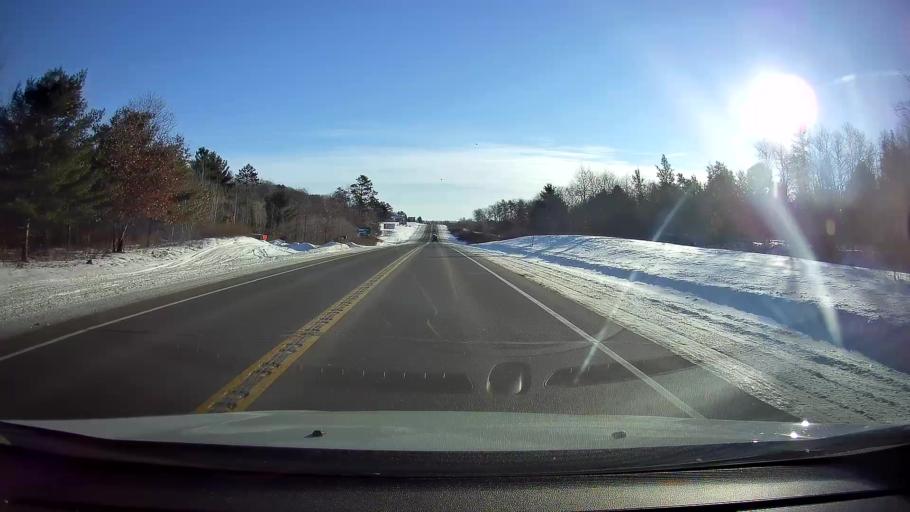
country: US
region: Wisconsin
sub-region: Sawyer County
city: Hayward
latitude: 45.9835
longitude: -91.5719
